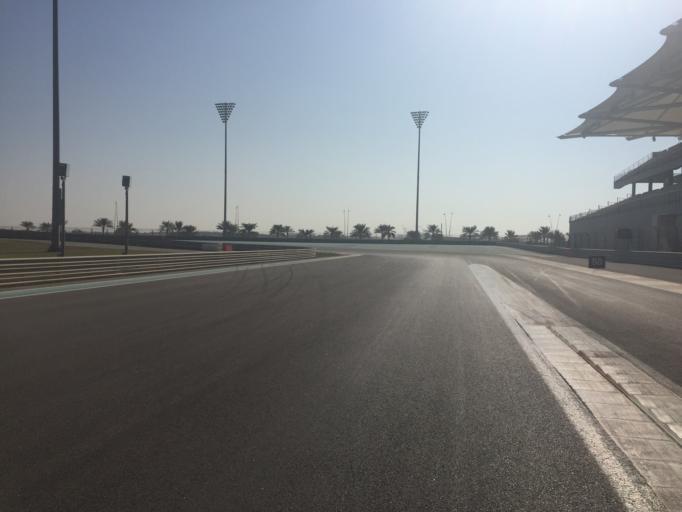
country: AE
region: Abu Dhabi
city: Abu Dhabi
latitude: 24.4633
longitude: 54.6082
